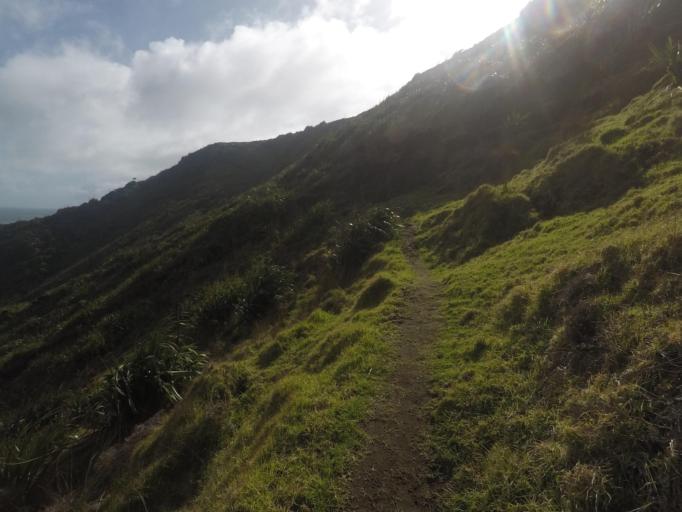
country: NZ
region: Auckland
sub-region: Auckland
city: Muriwai Beach
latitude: -36.8671
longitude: 174.4367
